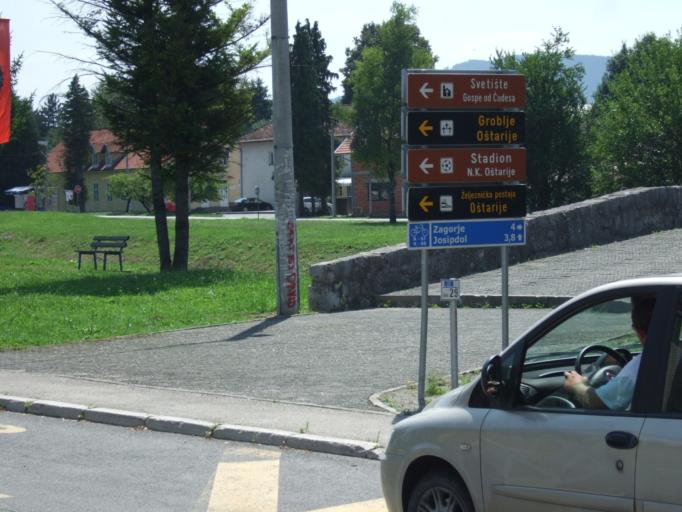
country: HR
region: Karlovacka
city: Ostarije
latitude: 45.2252
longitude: 15.2752
